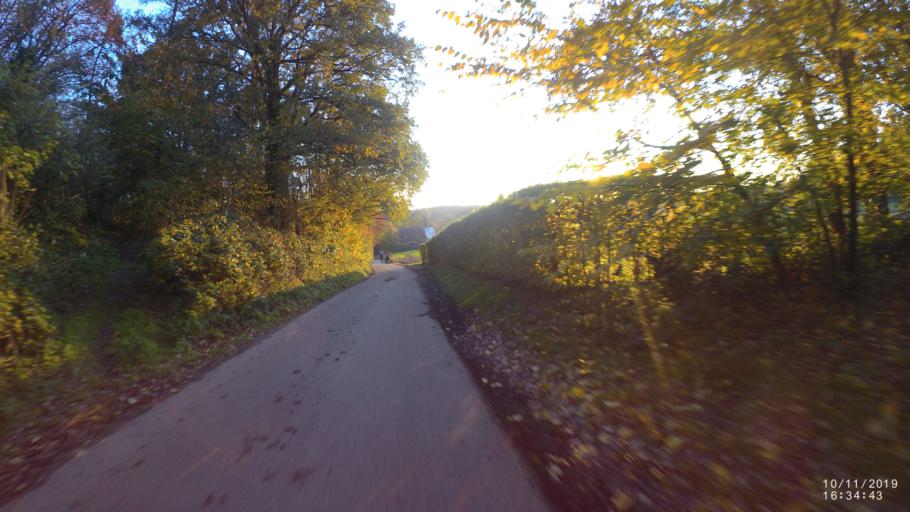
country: BE
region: Flanders
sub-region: Provincie Vlaams-Brabant
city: Lubbeek
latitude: 50.8704
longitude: 4.7894
